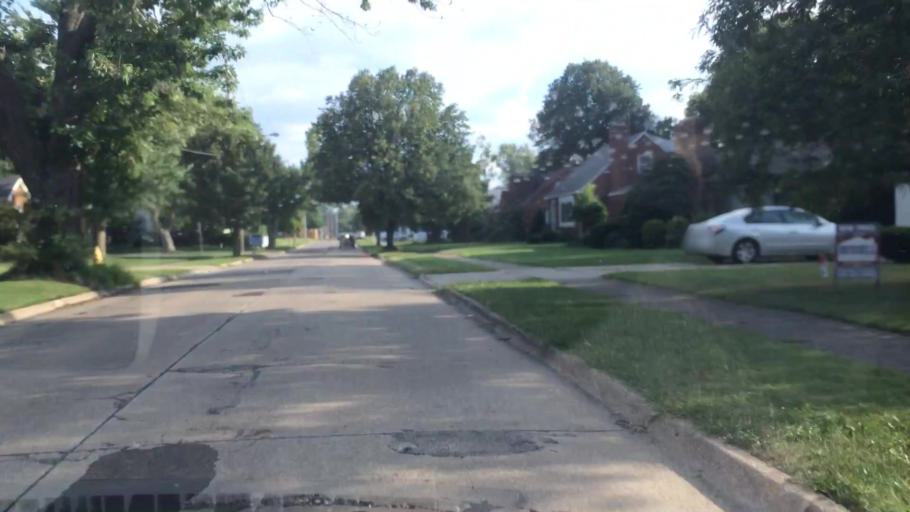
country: US
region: Ohio
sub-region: Cuyahoga County
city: Parma Heights
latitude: 41.4009
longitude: -81.7448
